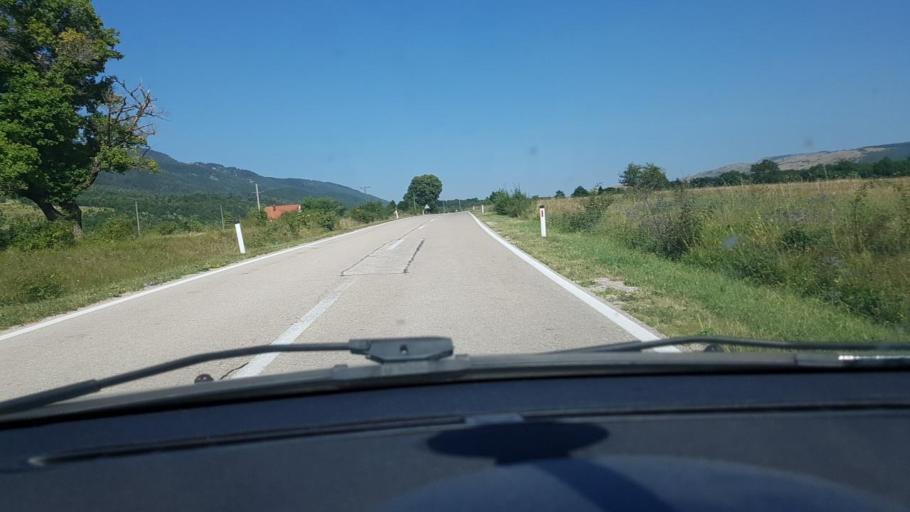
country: BA
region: Federation of Bosnia and Herzegovina
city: Bosansko Grahovo
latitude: 44.0935
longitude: 16.5605
